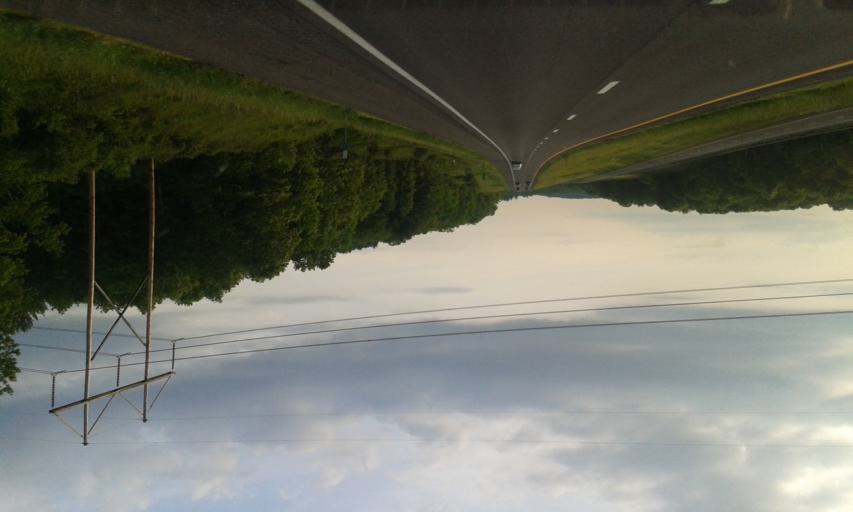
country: US
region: New York
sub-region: Broome County
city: Chenango Bridge
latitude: 42.2090
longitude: -75.9007
